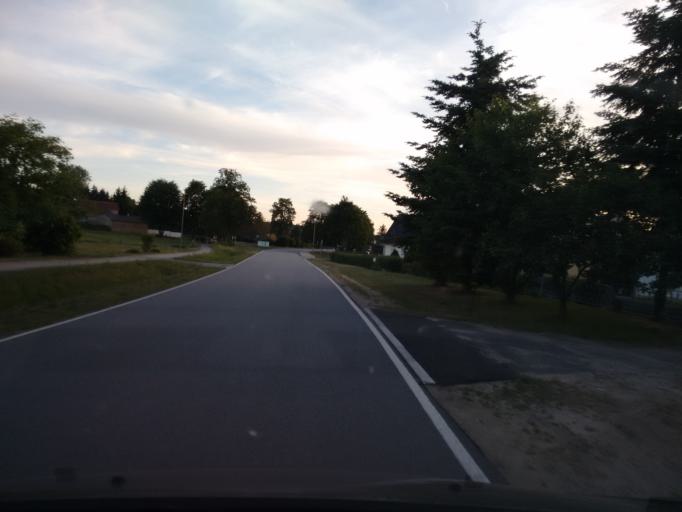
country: DE
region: Brandenburg
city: Gross Lindow
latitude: 52.1401
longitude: 14.4973
